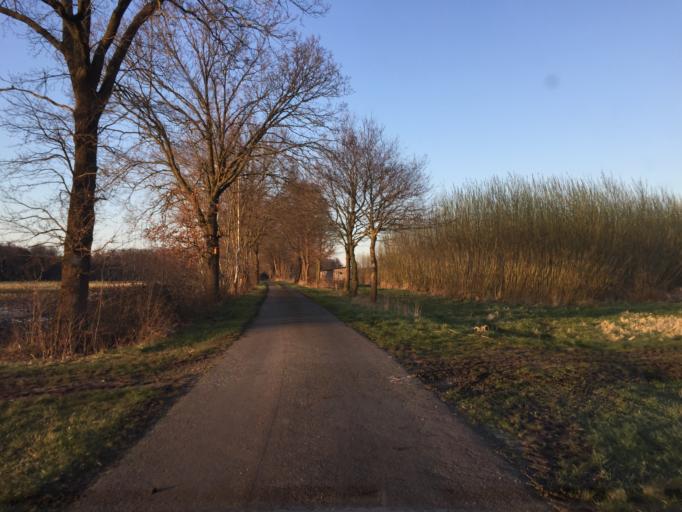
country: DE
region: Lower Saxony
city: Varrel
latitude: 52.6627
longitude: 8.7479
